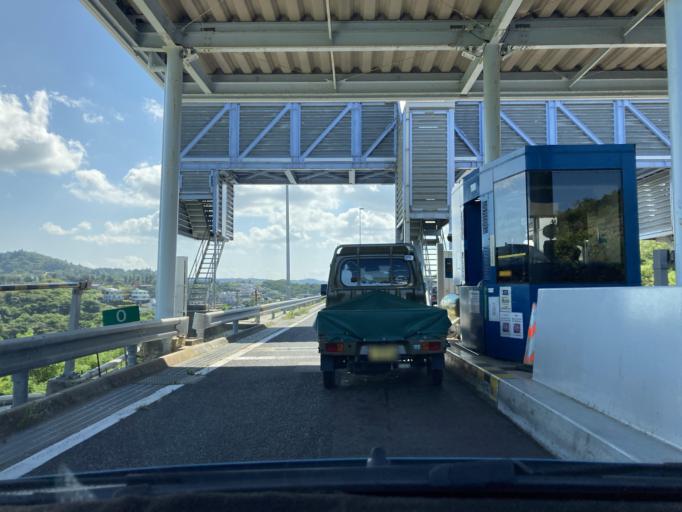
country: JP
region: Okinawa
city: Ginowan
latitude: 26.2216
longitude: 127.7390
